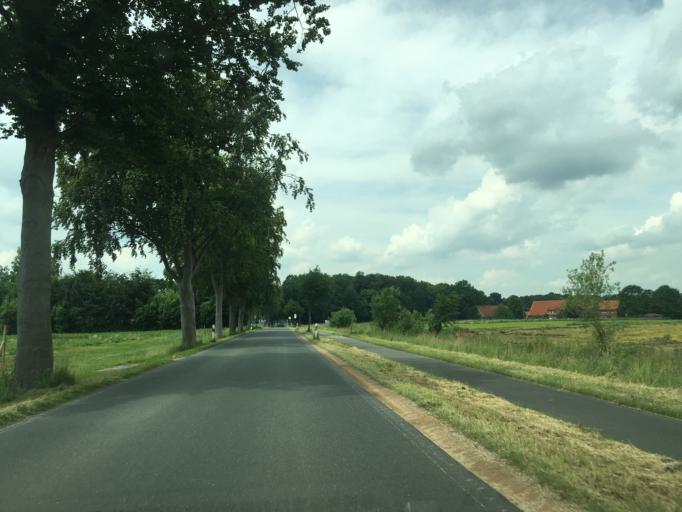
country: DE
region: North Rhine-Westphalia
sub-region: Regierungsbezirk Munster
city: Havixbeck
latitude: 51.9939
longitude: 7.4501
